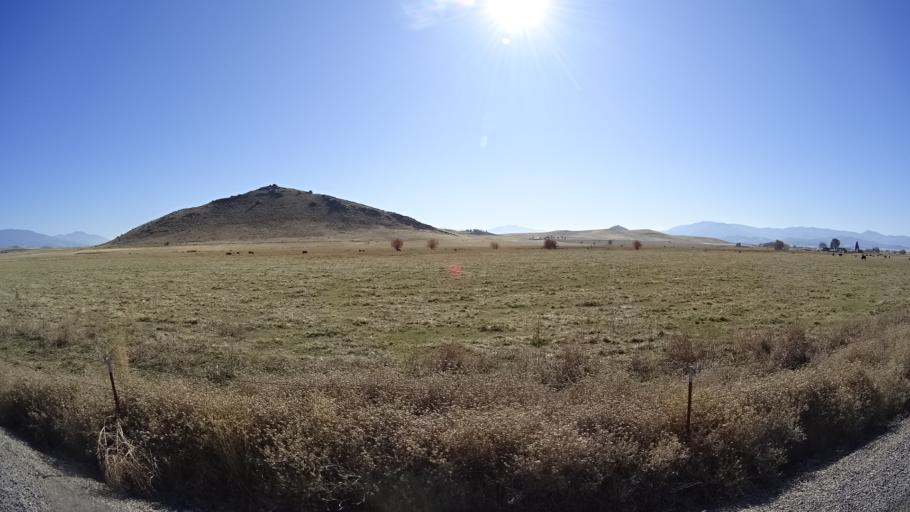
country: US
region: California
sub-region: Siskiyou County
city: Montague
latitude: 41.7567
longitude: -122.4914
